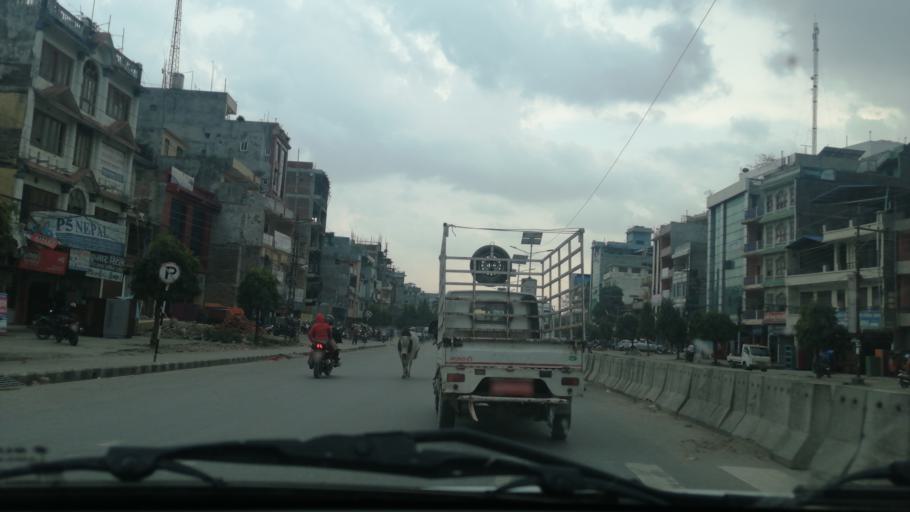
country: NP
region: Western Region
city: Butwal
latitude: 27.7004
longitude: 83.4659
